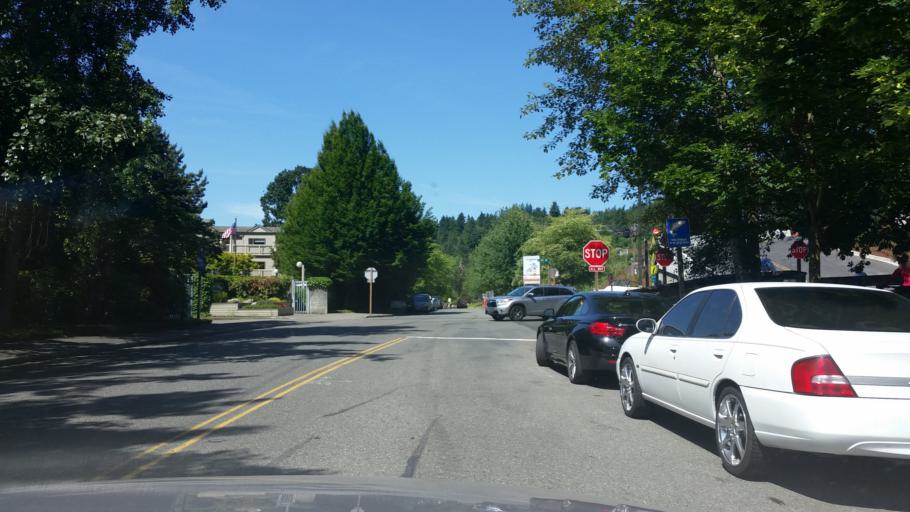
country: US
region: Washington
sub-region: King County
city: Kenmore
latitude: 47.7578
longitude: -122.2614
